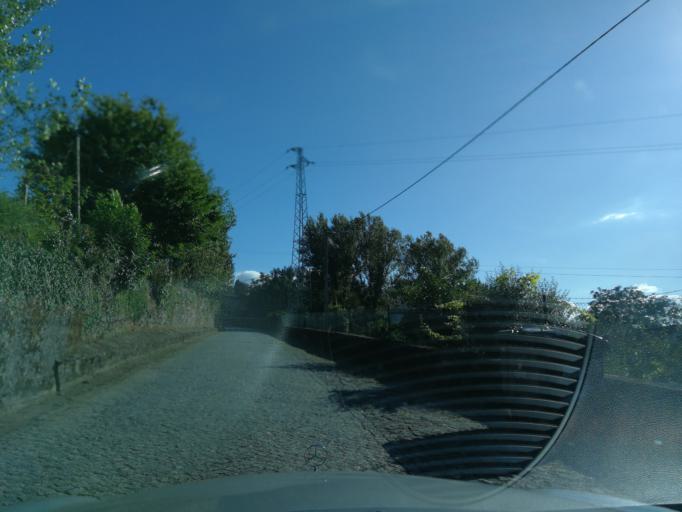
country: PT
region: Braga
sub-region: Braga
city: Adaufe
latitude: 41.5587
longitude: -8.3867
